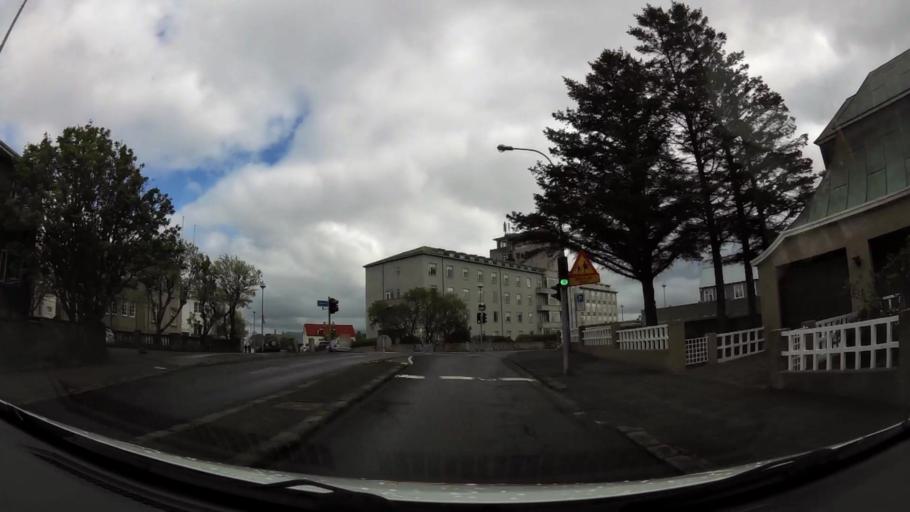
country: IS
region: Capital Region
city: Seltjarnarnes
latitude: 64.1479
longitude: -21.9509
